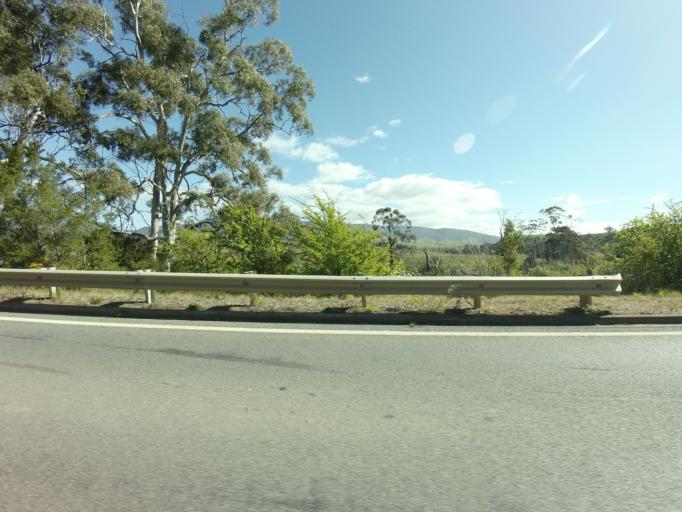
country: AU
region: Tasmania
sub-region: Derwent Valley
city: New Norfolk
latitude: -42.7341
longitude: 146.9744
